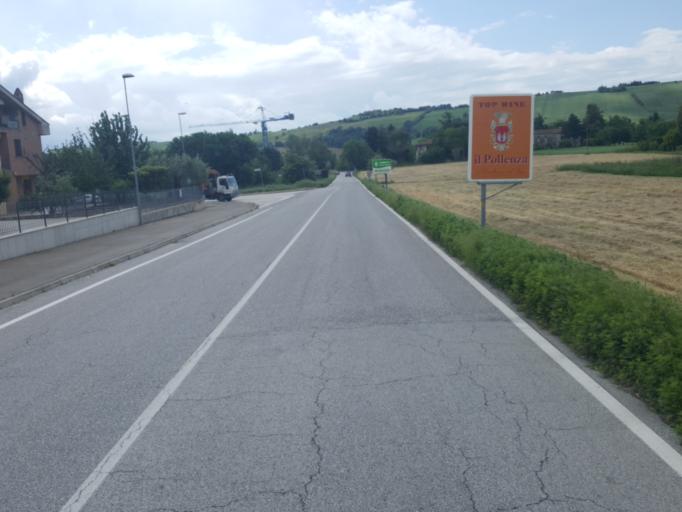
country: IT
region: The Marches
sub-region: Provincia di Macerata
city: Pollenza
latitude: 43.2383
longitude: 13.3659
